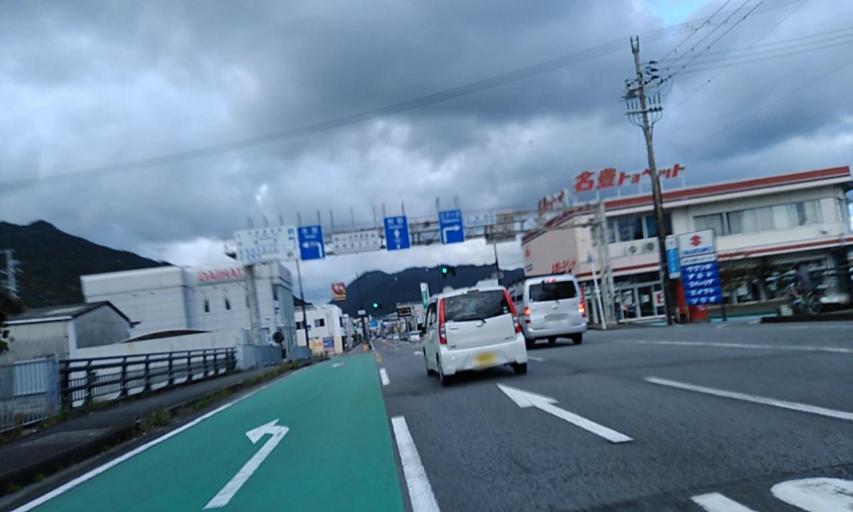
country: JP
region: Wakayama
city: Shingu
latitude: 33.7185
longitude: 135.9871
